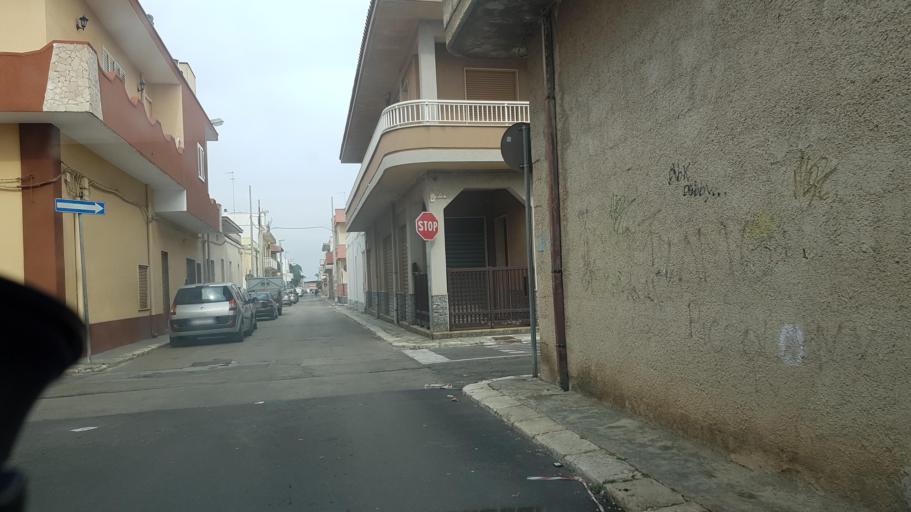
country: IT
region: Apulia
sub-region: Provincia di Brindisi
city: Cellino San Marco
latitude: 40.4730
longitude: 17.9650
